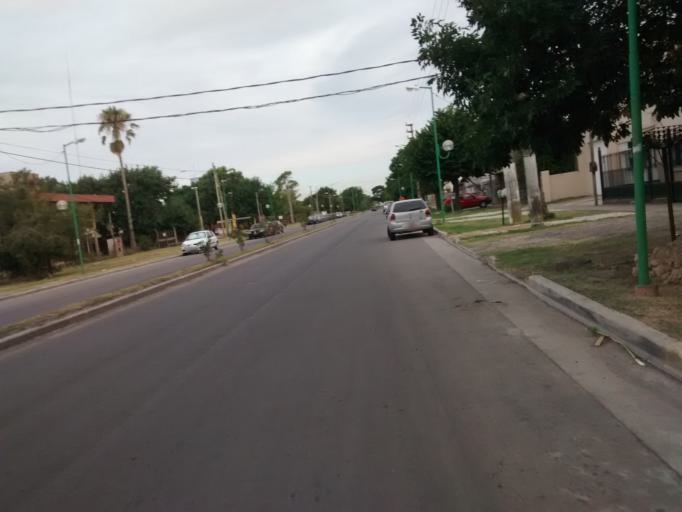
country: AR
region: Buenos Aires
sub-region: Partido de La Plata
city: La Plata
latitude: -34.9065
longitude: -58.0159
